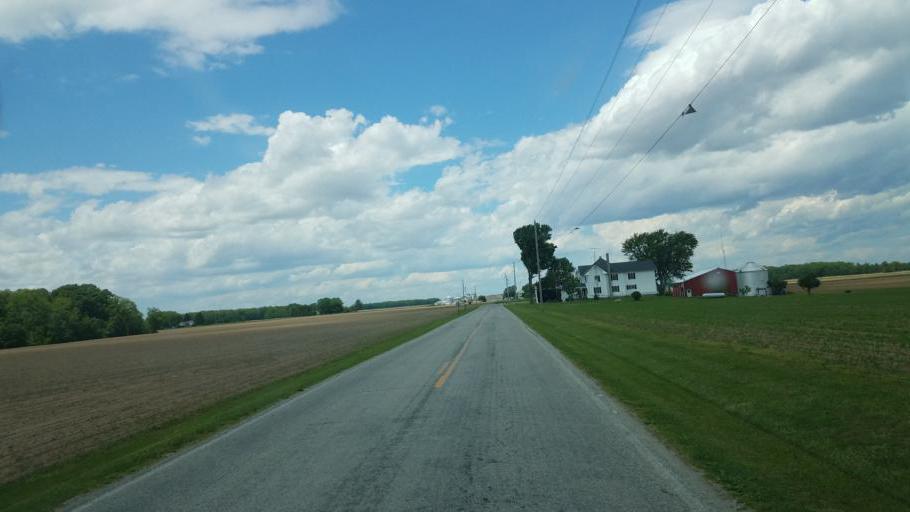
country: US
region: Ohio
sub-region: Huron County
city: Monroeville
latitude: 41.1929
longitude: -82.7299
